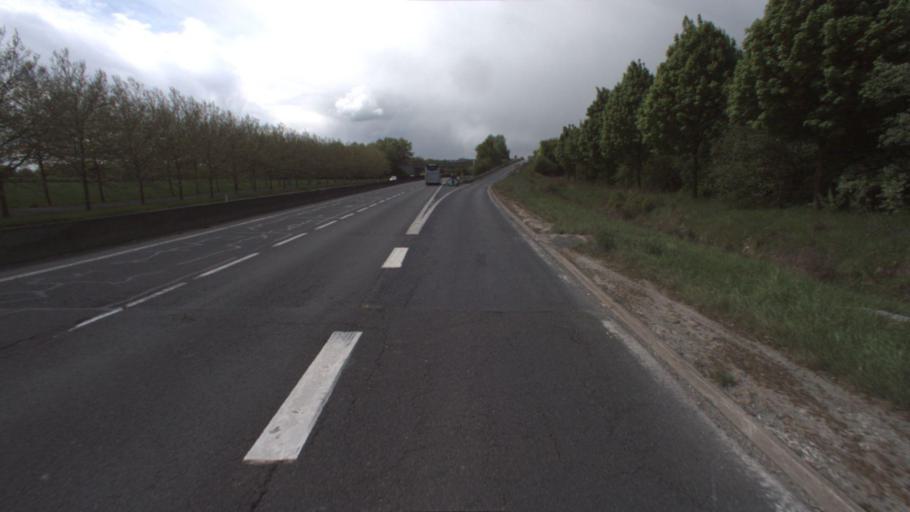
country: FR
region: Ile-de-France
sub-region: Departement de Seine-et-Marne
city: Tournan-en-Brie
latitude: 48.7336
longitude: 2.7815
